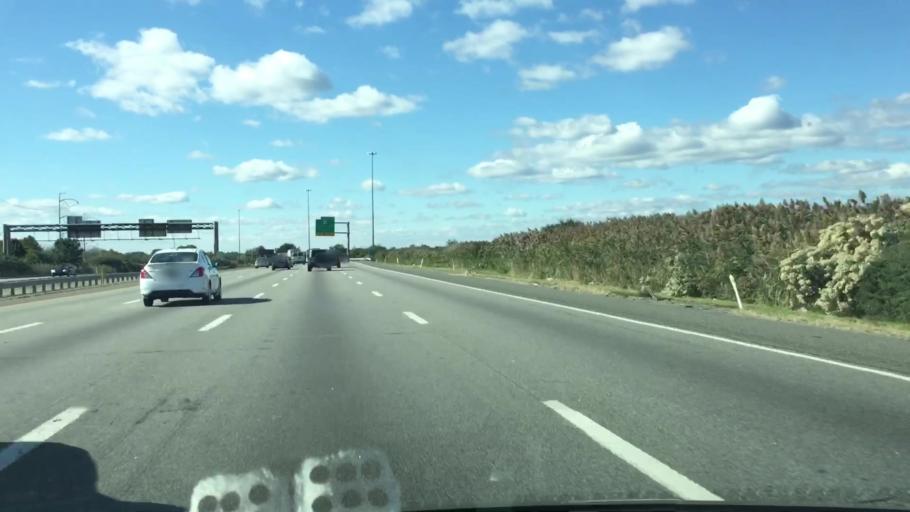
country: US
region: Pennsylvania
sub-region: Delaware County
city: Folcroft
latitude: 39.8764
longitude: -75.2780
